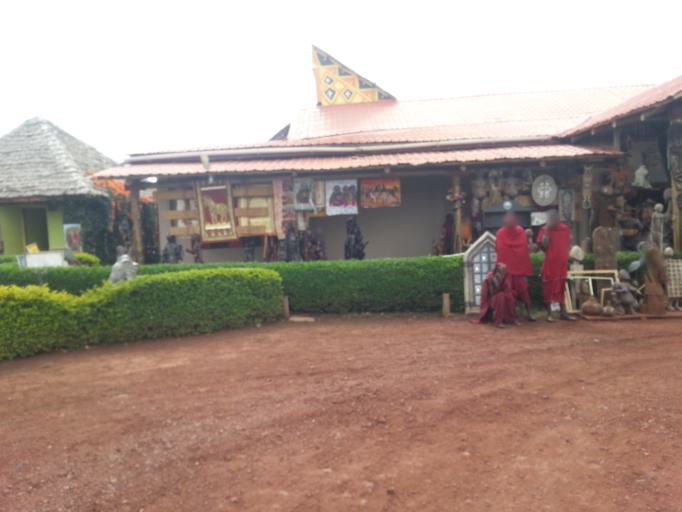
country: TZ
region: Arusha
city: Mto wa Mbu
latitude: -3.3680
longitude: 35.8071
